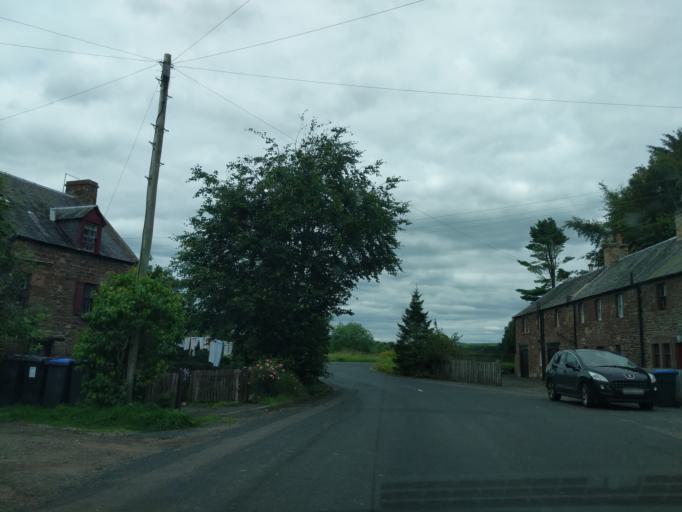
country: GB
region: Scotland
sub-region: The Scottish Borders
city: West Linton
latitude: 55.7185
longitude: -3.3375
